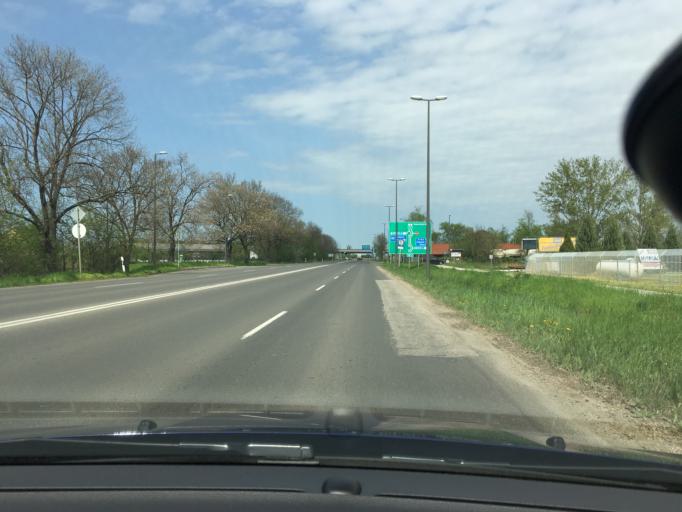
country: HU
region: Csongrad
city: Szeged
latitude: 46.2907
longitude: 20.1743
